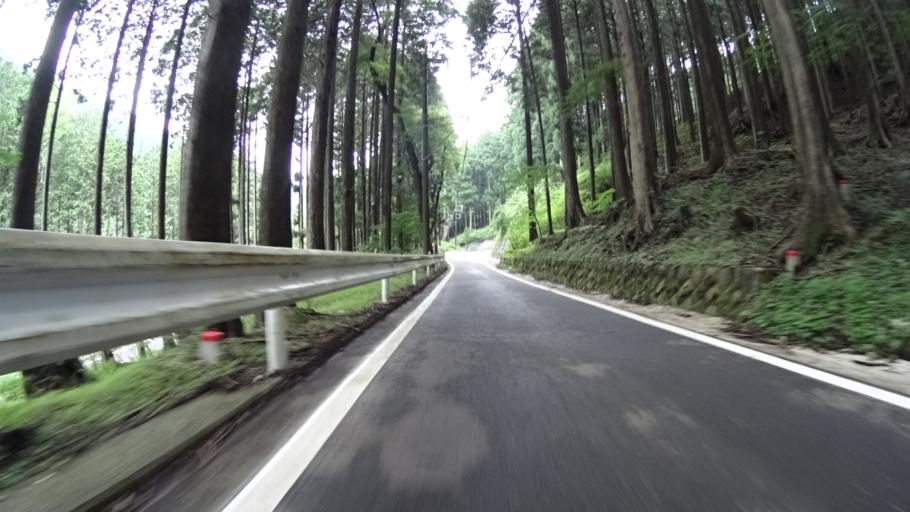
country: JP
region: Kanagawa
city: Hadano
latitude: 35.4449
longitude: 139.2132
